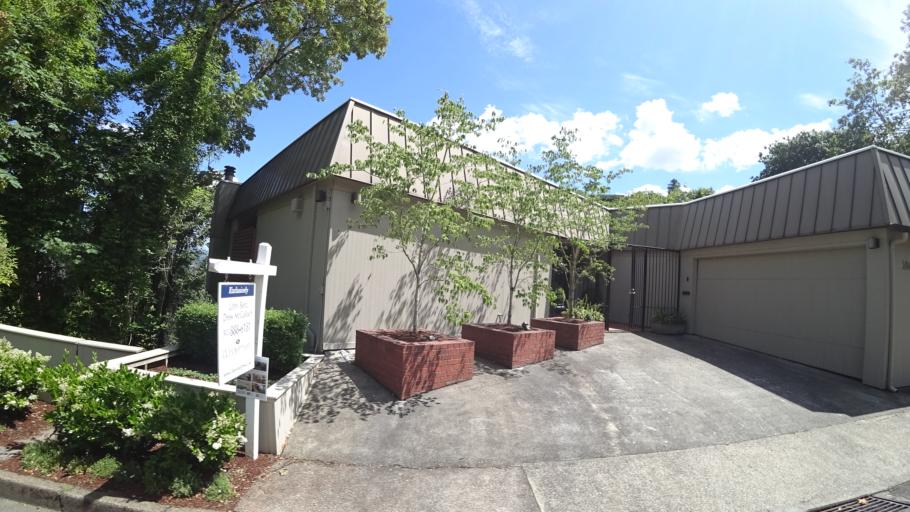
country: US
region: Oregon
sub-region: Multnomah County
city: Portland
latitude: 45.5089
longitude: -122.6905
